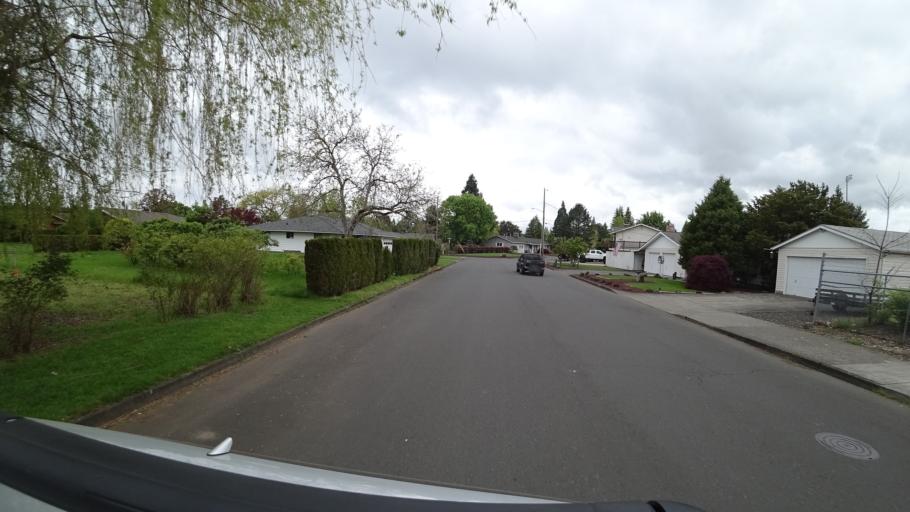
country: US
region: Oregon
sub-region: Washington County
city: Hillsboro
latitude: 45.5286
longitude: -122.9748
